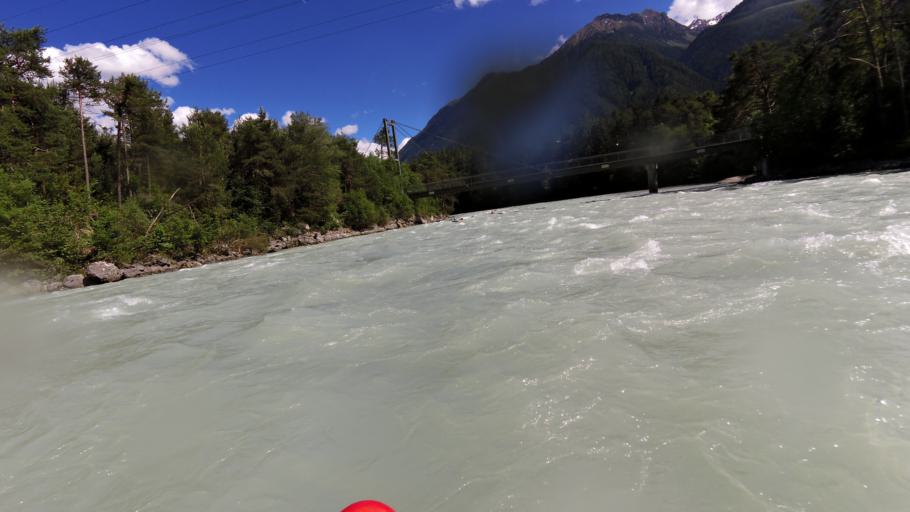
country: AT
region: Tyrol
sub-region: Politischer Bezirk Imst
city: Roppen
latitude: 47.2273
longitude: 10.8234
